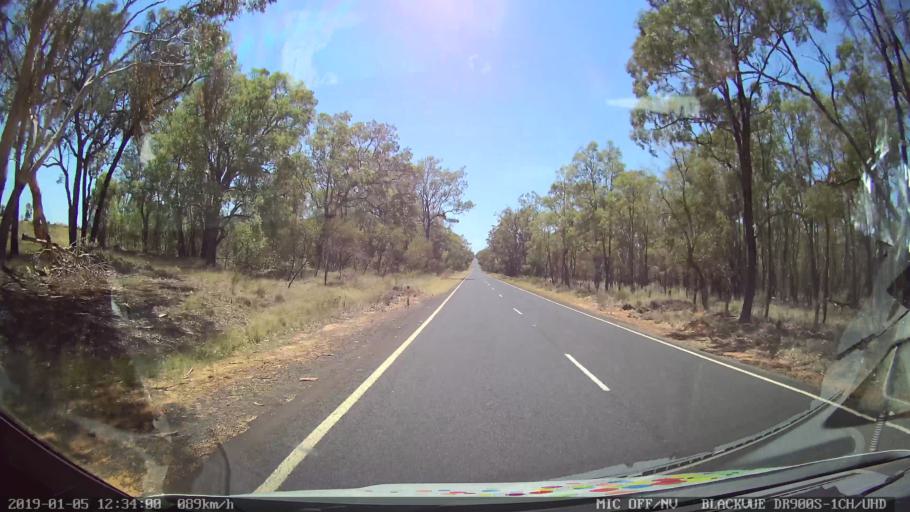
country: AU
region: New South Wales
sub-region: Warrumbungle Shire
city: Coonabarabran
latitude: -31.2133
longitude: 149.4034
